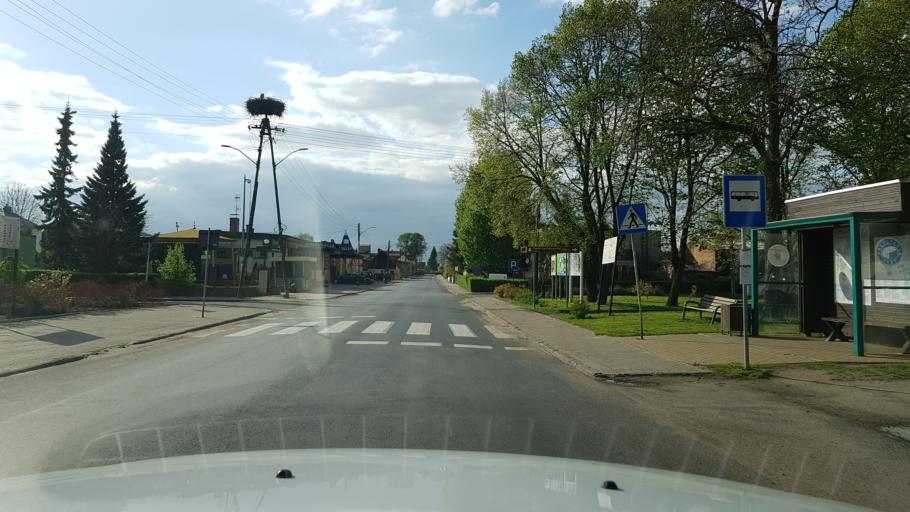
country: PL
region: West Pomeranian Voivodeship
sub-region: Powiat pyrzycki
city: Przelewice
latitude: 53.1046
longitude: 15.0769
